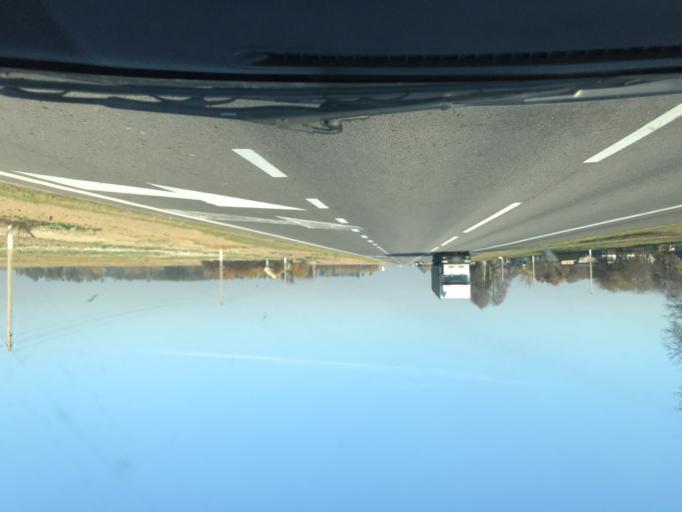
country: BY
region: Vitebsk
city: Orsha
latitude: 54.3384
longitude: 30.4462
